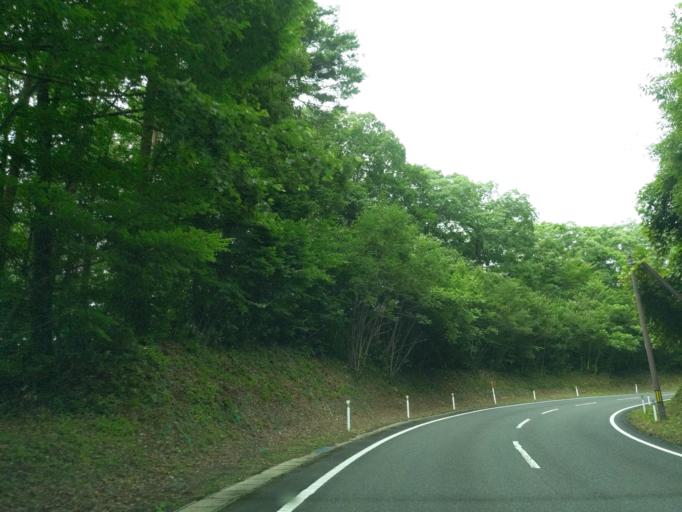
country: JP
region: Tochigi
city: Kuroiso
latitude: 37.2518
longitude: 140.0792
